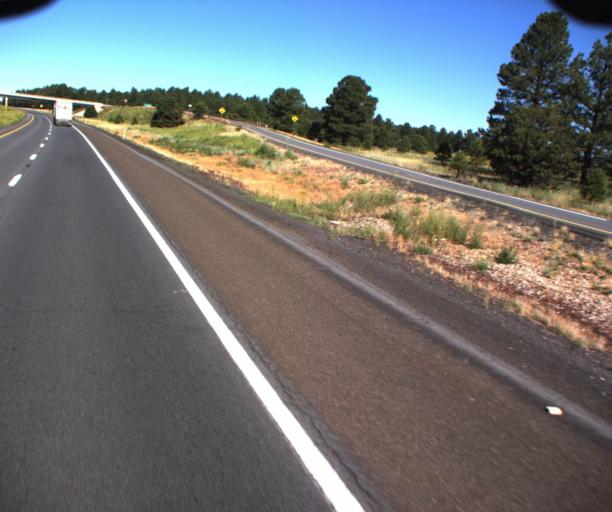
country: US
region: Arizona
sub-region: Coconino County
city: Parks
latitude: 35.2643
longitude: -112.0470
